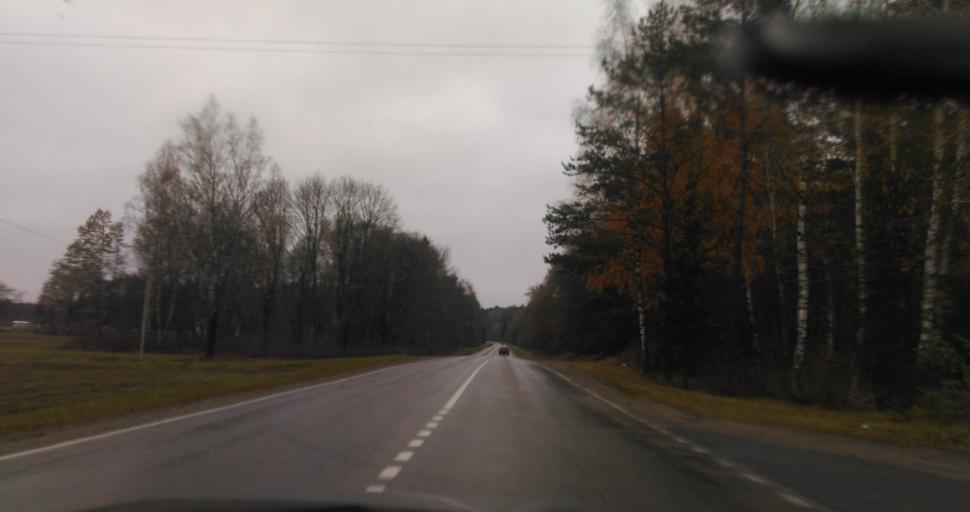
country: LT
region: Panevezys
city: Rokiskis
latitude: 55.8597
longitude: 25.5422
